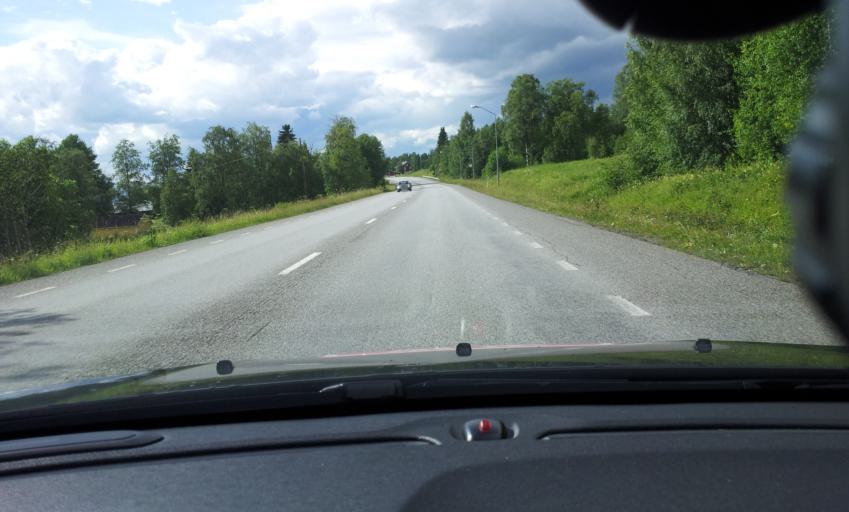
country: SE
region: Jaemtland
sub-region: Are Kommun
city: Jarpen
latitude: 63.3133
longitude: 13.5985
